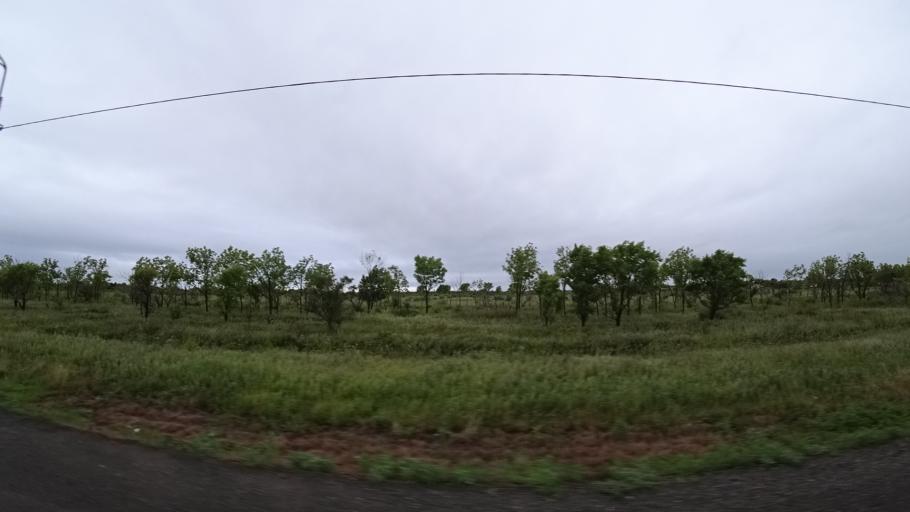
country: RU
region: Primorskiy
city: Chernigovka
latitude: 44.3260
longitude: 132.5714
